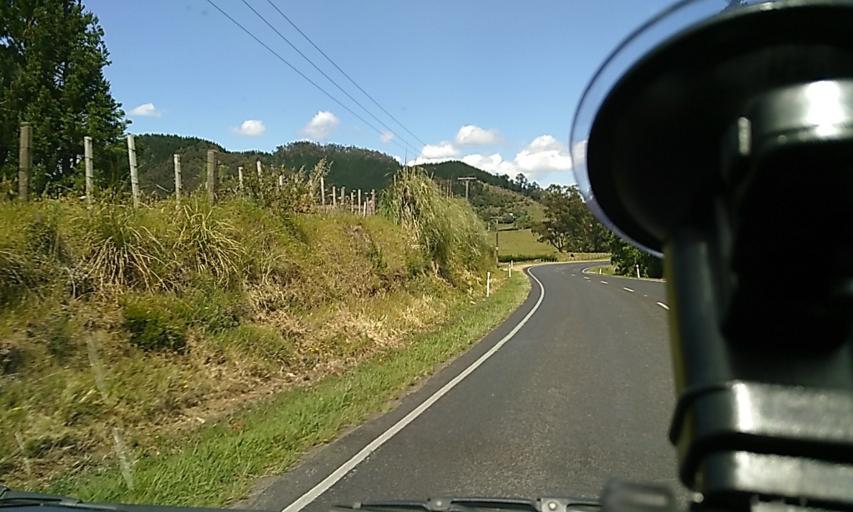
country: NZ
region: Bay of Plenty
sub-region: Western Bay of Plenty District
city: Waihi Beach
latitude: -37.4560
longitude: 175.9371
